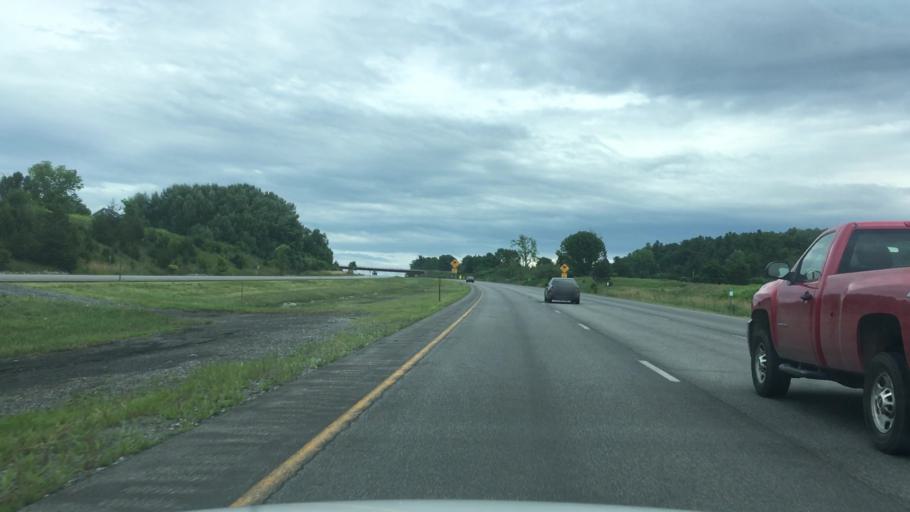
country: US
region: New York
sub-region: Schoharie County
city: Schoharie
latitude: 42.7121
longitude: -74.2841
